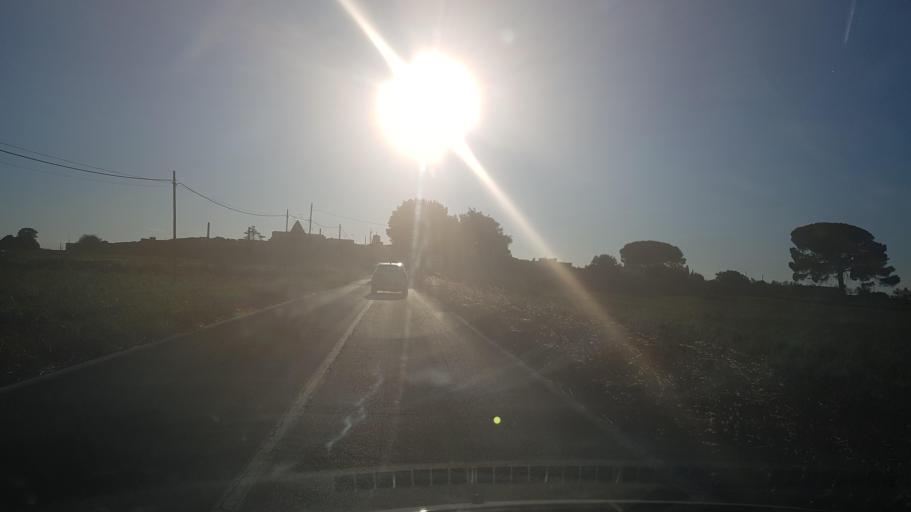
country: IT
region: Apulia
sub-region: Provincia di Lecce
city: Vernole
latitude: 40.3219
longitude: 18.3232
